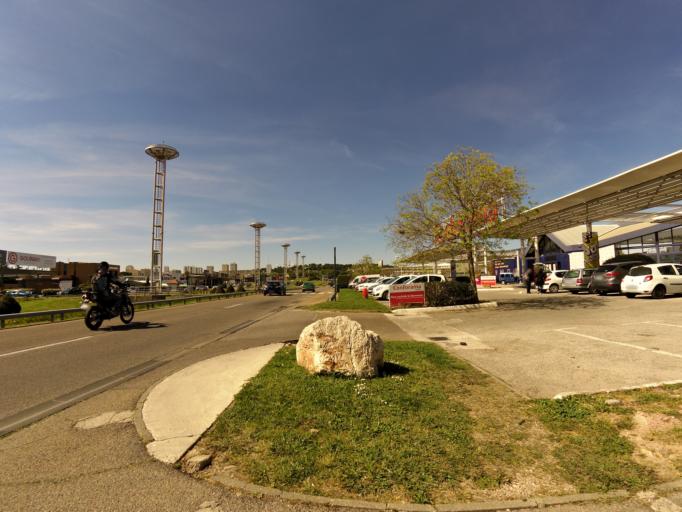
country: FR
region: Languedoc-Roussillon
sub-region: Departement du Gard
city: Nimes
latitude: 43.8149
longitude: 4.3495
